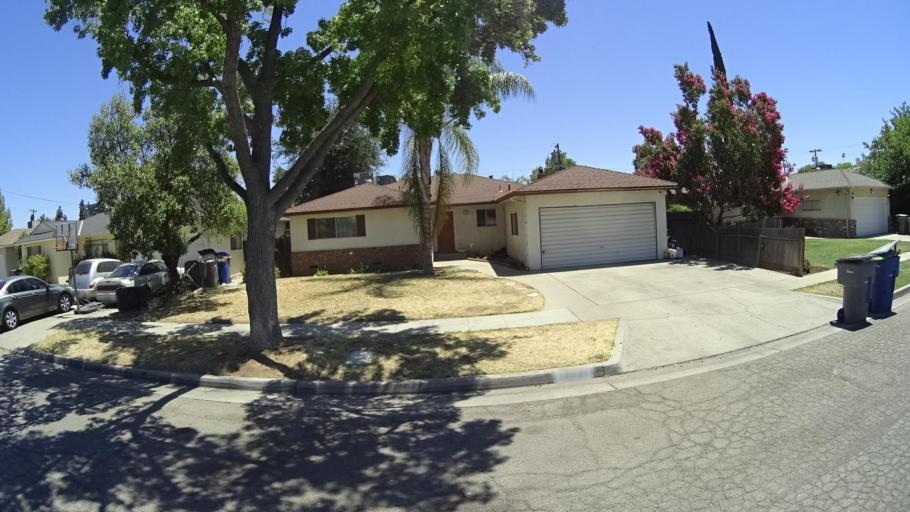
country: US
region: California
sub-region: Fresno County
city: Fresno
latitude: 36.8021
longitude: -119.7696
